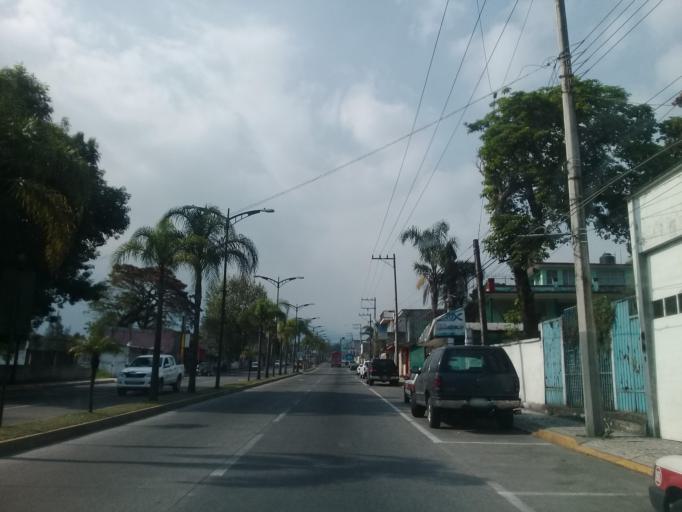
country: MX
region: Veracruz
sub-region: Ixhuatlancillo
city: Union y Progreso
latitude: 18.8660
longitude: -97.1119
